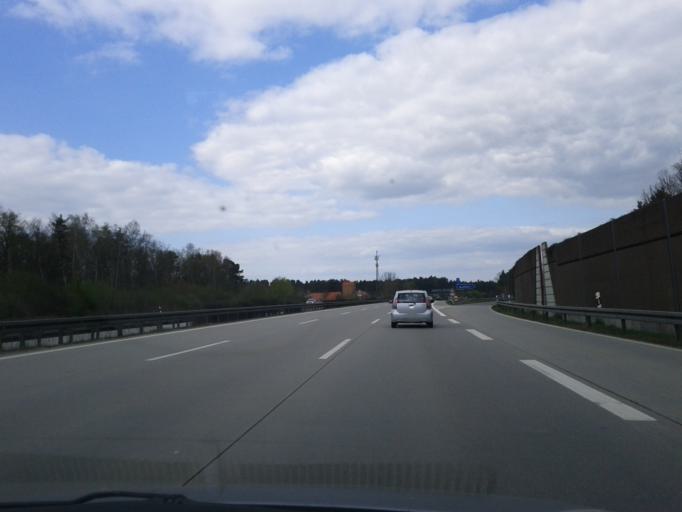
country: DE
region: Brandenburg
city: Grunheide
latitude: 52.4202
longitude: 13.7855
